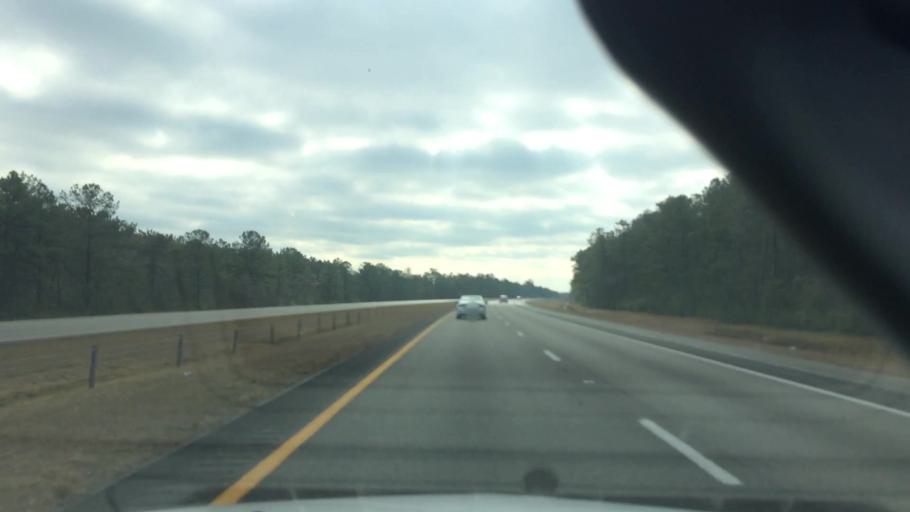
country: US
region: North Carolina
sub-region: New Hanover County
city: Castle Hayne
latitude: 34.3908
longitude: -77.8755
